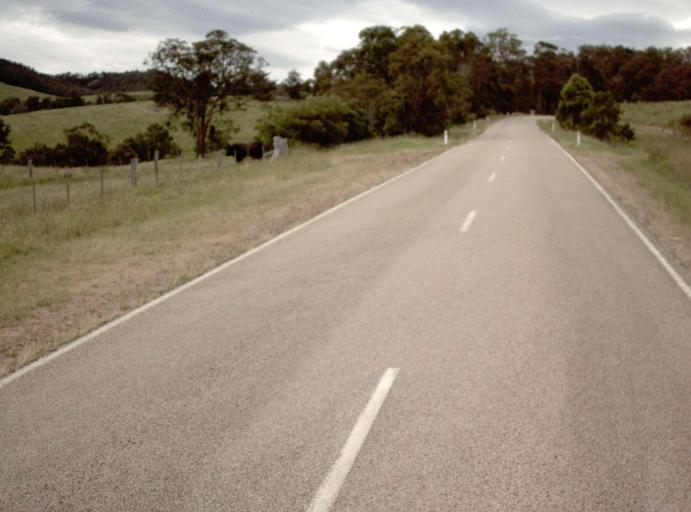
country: AU
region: Victoria
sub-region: East Gippsland
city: Bairnsdale
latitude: -37.5851
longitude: 147.1835
